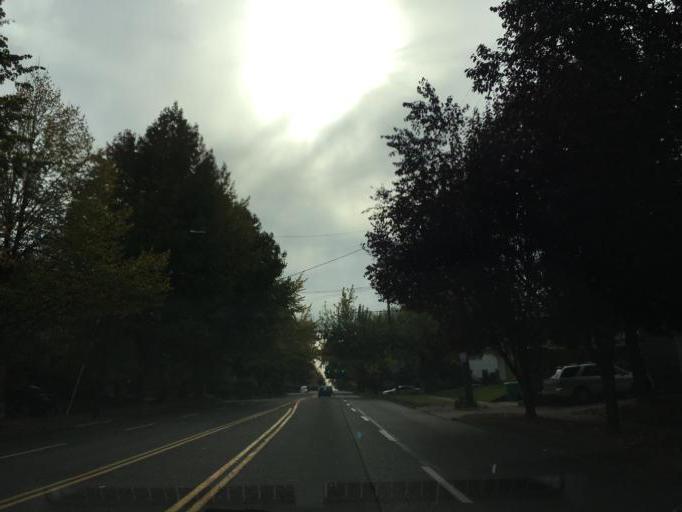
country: US
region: Oregon
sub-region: Multnomah County
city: Portland
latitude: 45.5301
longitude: -122.6230
